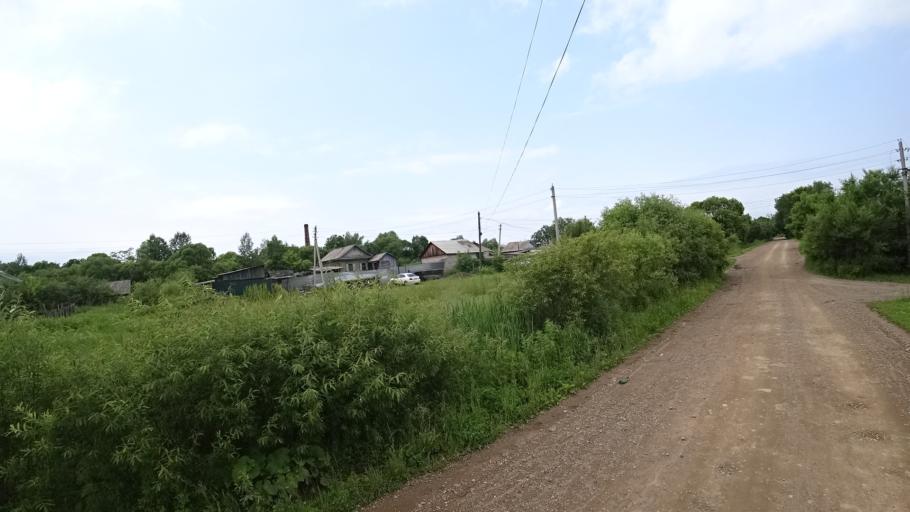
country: RU
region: Primorskiy
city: Novosysoyevka
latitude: 44.2287
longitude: 133.3670
